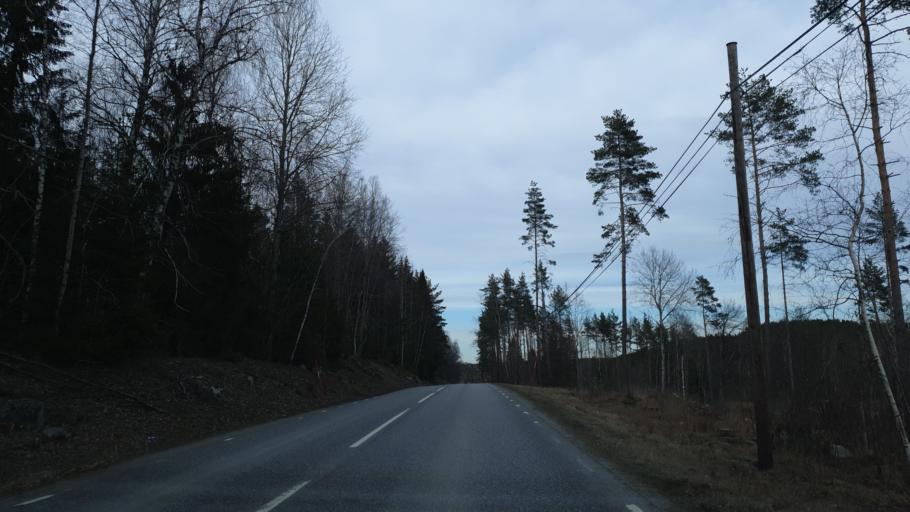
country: SE
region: Stockholm
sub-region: Osterakers Kommun
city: Akersberga
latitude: 59.5913
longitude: 18.3004
